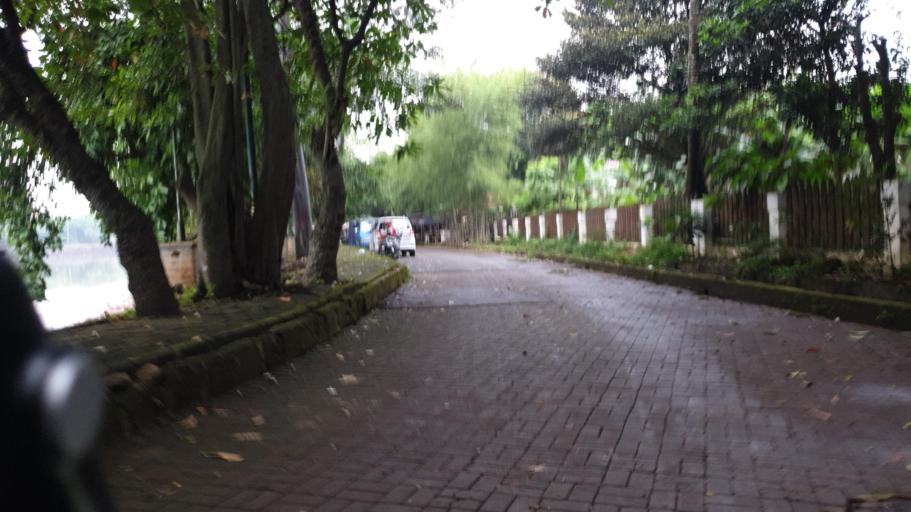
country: ID
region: West Java
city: Depok
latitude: -6.3417
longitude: 106.8215
